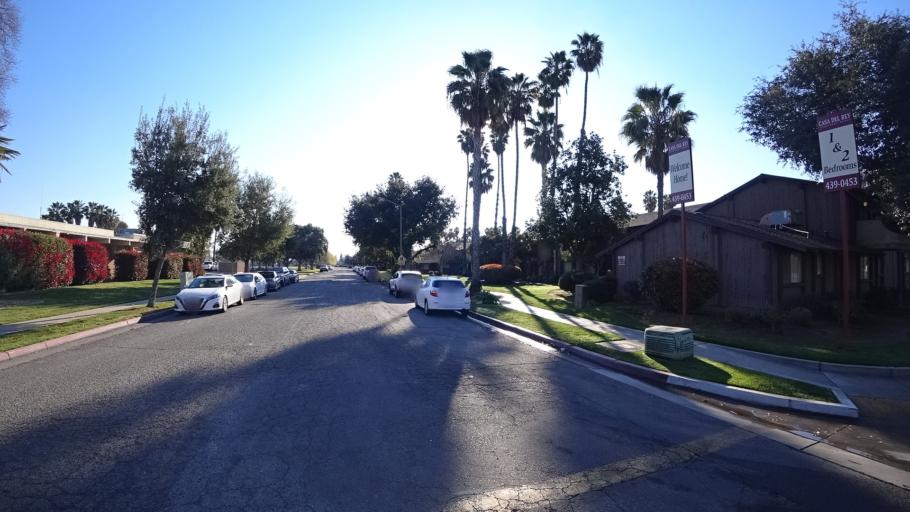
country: US
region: California
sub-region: Fresno County
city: Fresno
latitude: 36.8176
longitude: -119.7812
